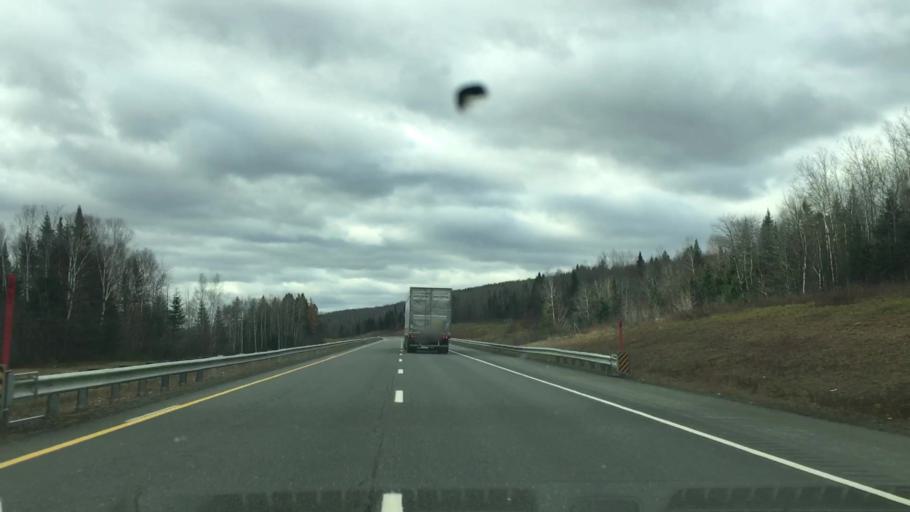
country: US
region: Maine
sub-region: Aroostook County
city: Fort Fairfield
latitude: 46.6544
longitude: -67.7378
